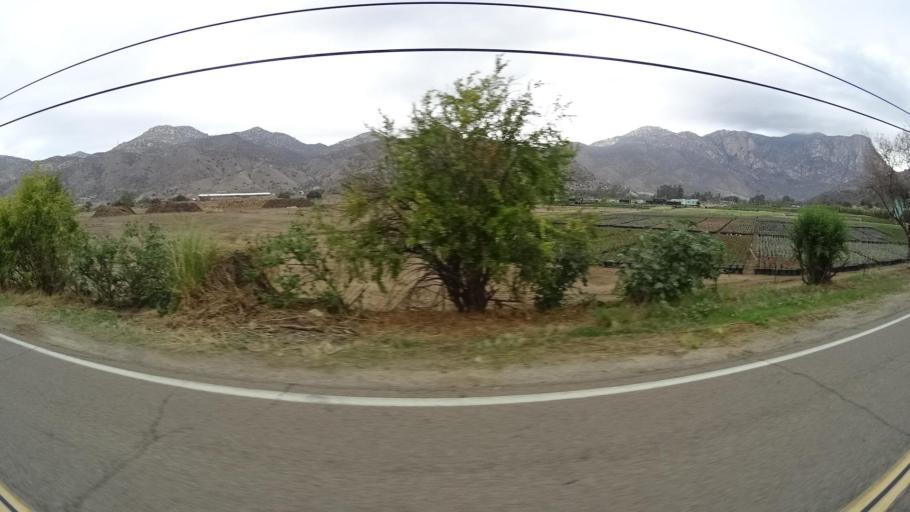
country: US
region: California
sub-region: San Diego County
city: Lakeside
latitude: 32.8759
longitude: -116.8645
